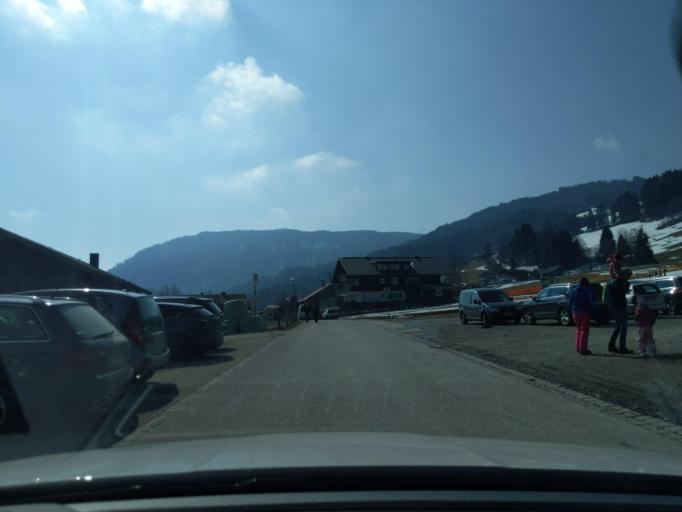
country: DE
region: Bavaria
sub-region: Swabia
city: Obermaiselstein
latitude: 47.4570
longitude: 10.2321
